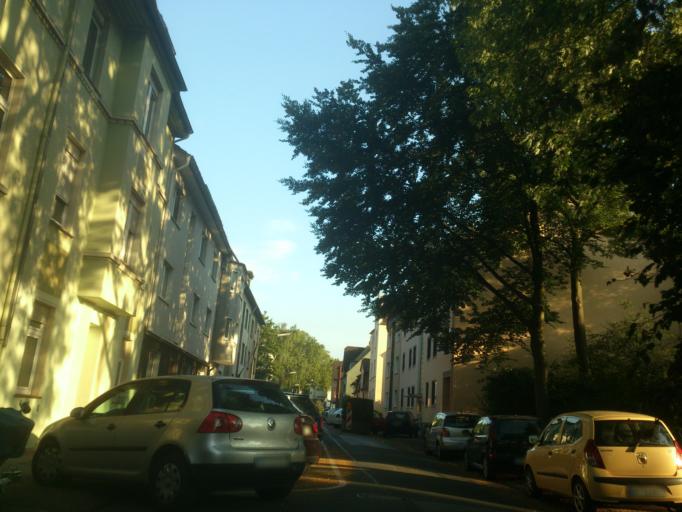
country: DE
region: North Rhine-Westphalia
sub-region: Regierungsbezirk Arnsberg
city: Dortmund
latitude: 51.4844
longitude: 7.4357
